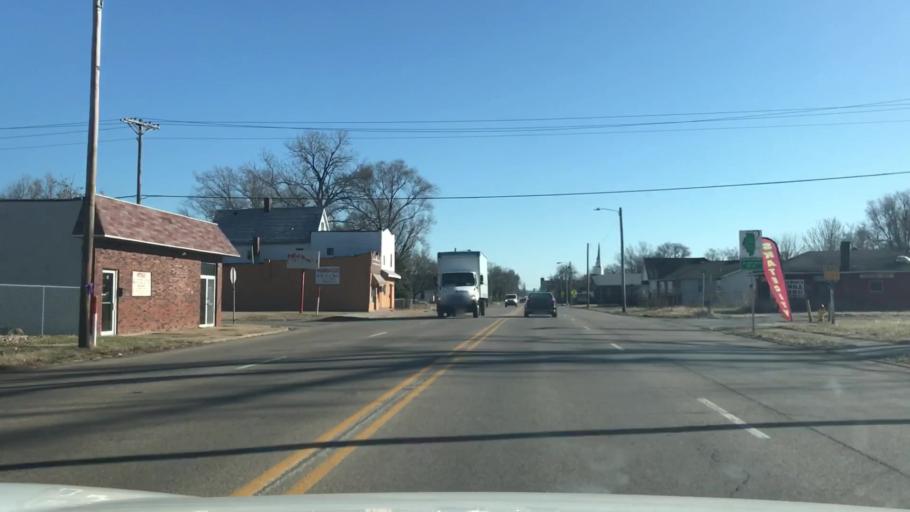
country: US
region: Illinois
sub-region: Saint Clair County
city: East Saint Louis
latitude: 38.6084
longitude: -90.1380
